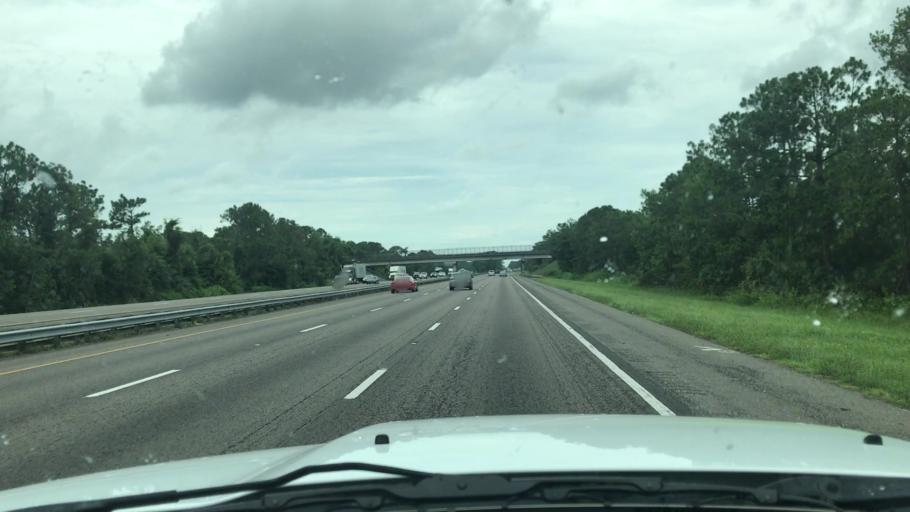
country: US
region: Florida
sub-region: Volusia County
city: Ormond Beach
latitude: 29.2716
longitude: -81.1209
